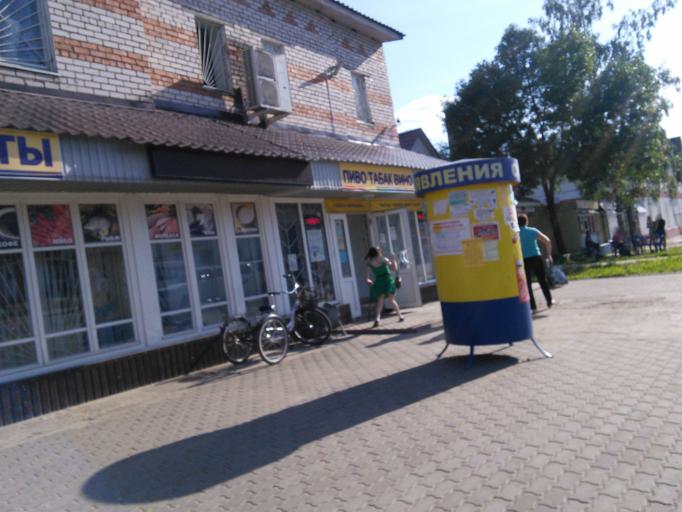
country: RU
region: Vologda
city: Chagoda
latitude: 59.1640
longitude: 35.3277
